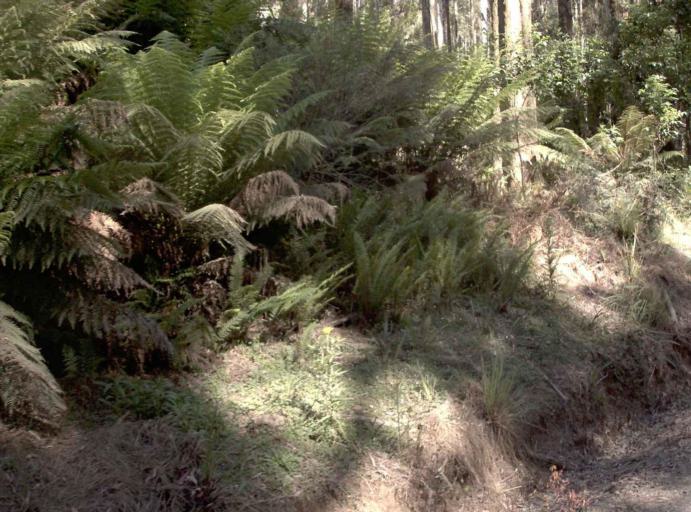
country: AU
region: New South Wales
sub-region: Bombala
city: Bombala
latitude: -37.2408
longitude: 148.7568
